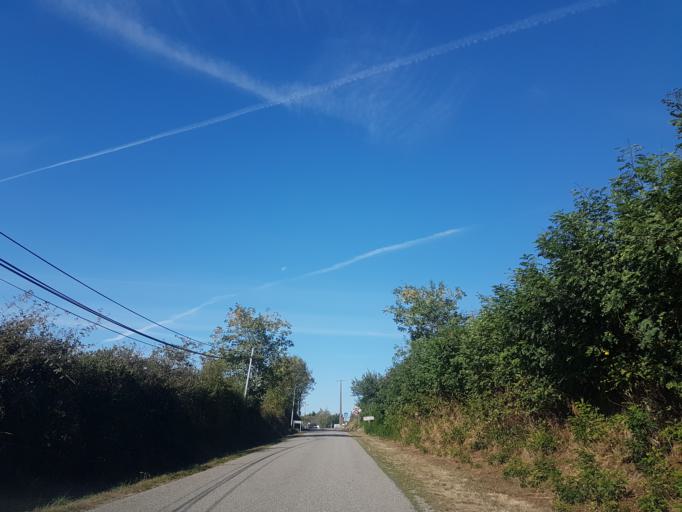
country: FR
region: Pays de la Loire
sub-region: Departement de la Loire-Atlantique
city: Petit-Mars
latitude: 47.3929
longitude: -1.4497
